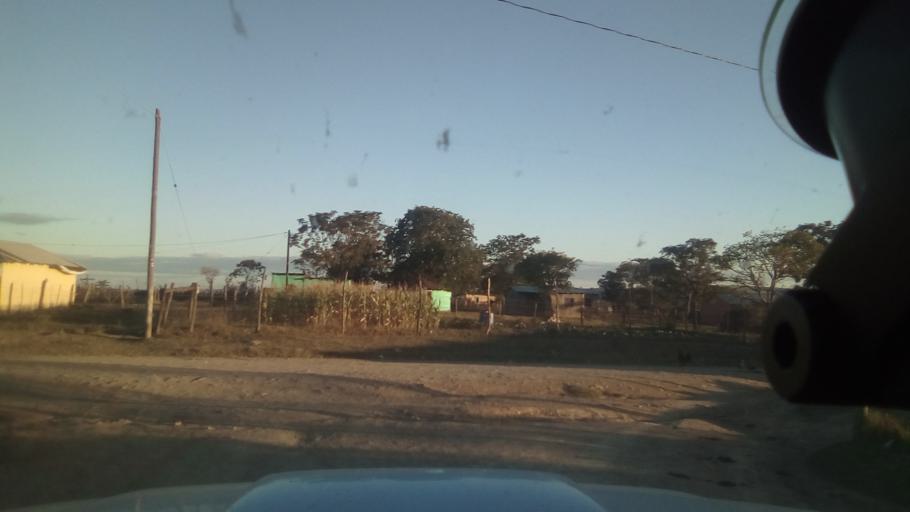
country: ZA
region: Eastern Cape
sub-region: Buffalo City Metropolitan Municipality
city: Bhisho
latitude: -32.7374
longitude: 27.3774
